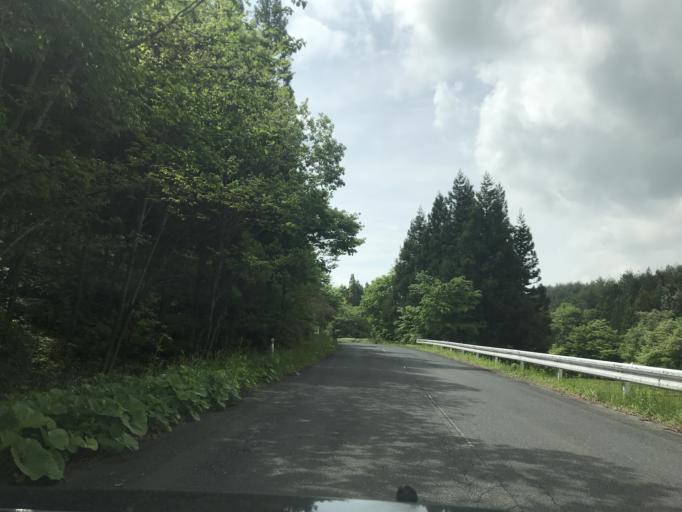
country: JP
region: Iwate
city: Ichinoseki
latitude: 38.8784
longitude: 140.9754
